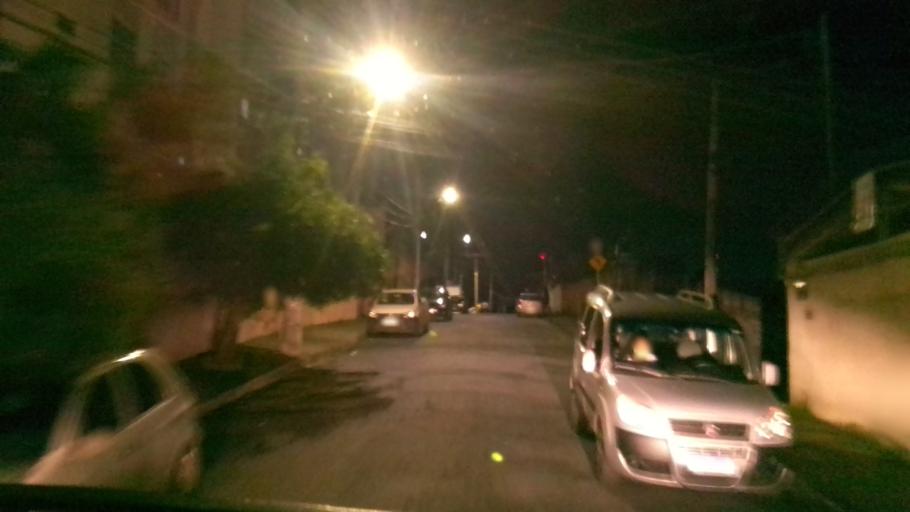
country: BR
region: Minas Gerais
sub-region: Belo Horizonte
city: Belo Horizonte
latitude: -19.8995
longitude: -43.9786
